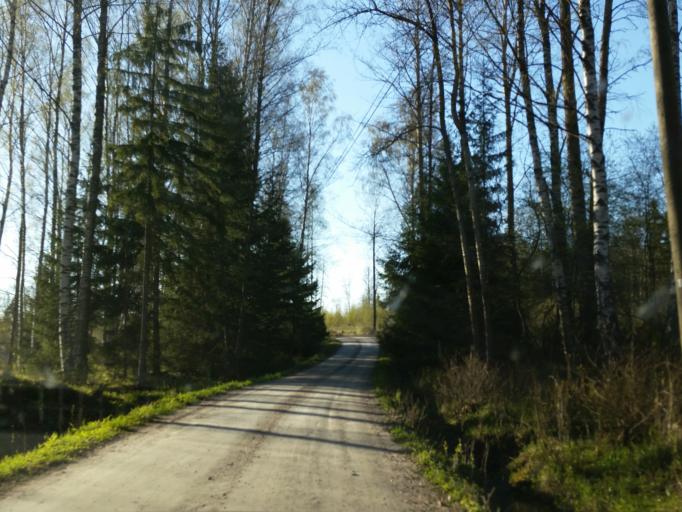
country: FI
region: Uusimaa
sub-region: Helsinki
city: Espoo
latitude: 60.1146
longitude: 24.6225
